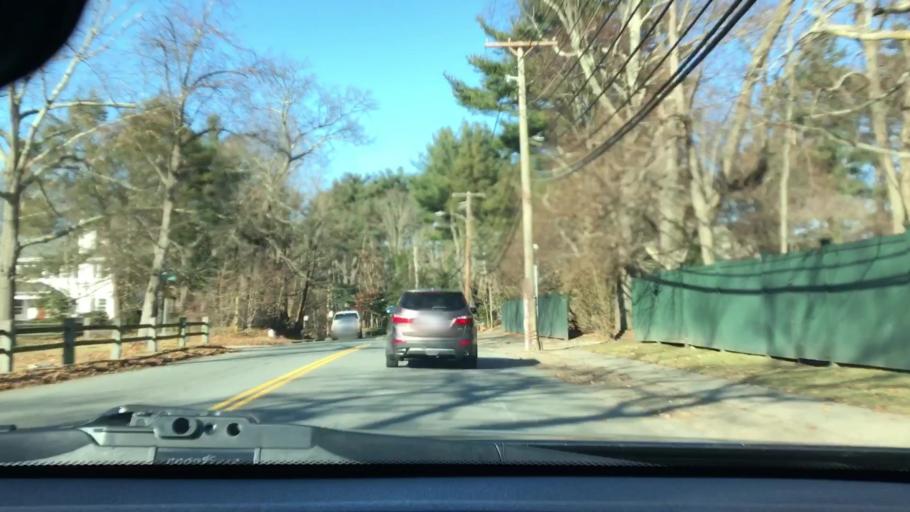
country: US
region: Massachusetts
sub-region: Norfolk County
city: Dedham
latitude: 42.2523
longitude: -71.1846
